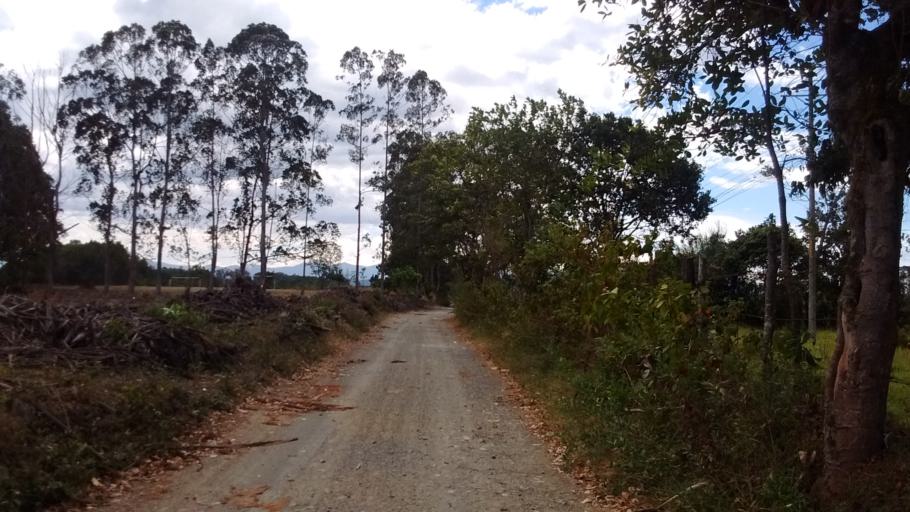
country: CO
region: Cauca
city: Popayan
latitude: 2.4953
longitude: -76.5905
